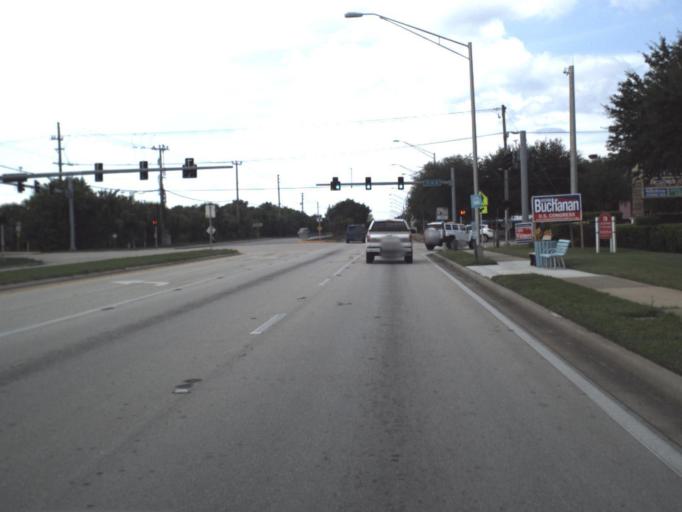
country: US
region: Florida
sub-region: Manatee County
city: West Bradenton
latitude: 27.4626
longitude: -82.6360
